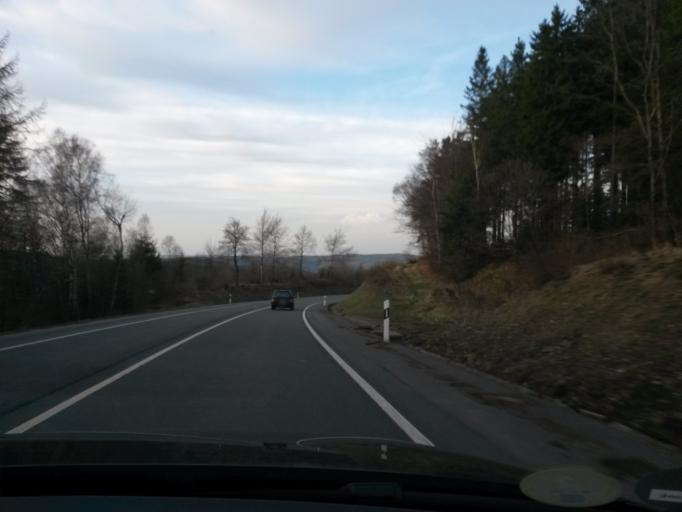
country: DE
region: North Rhine-Westphalia
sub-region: Regierungsbezirk Arnsberg
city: Herscheid
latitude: 51.1476
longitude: 7.7458
